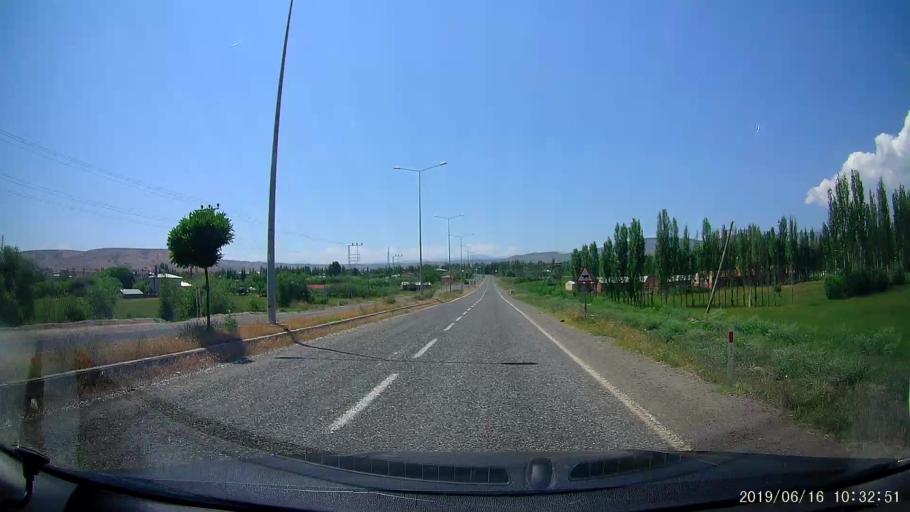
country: TR
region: Igdir
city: Tuzluca
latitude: 40.0462
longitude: 43.6545
